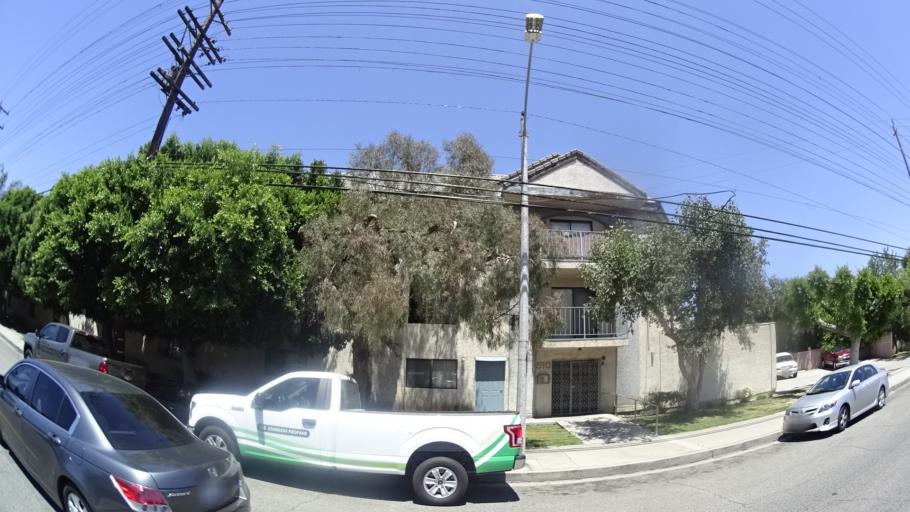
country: US
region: California
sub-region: Los Angeles County
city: Burbank
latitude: 34.1723
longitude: -118.3100
